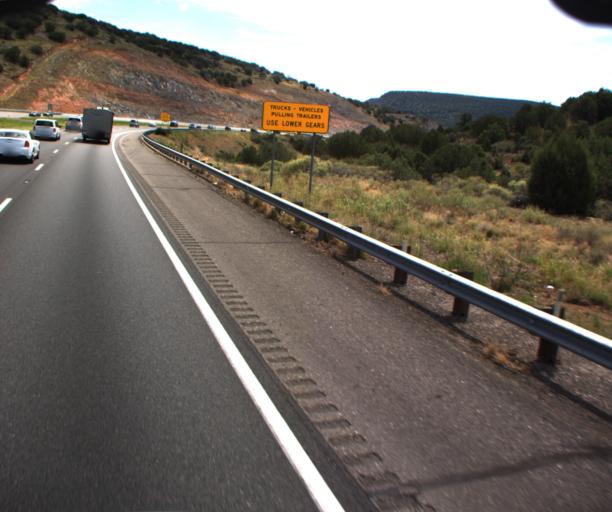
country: US
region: Arizona
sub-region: Yavapai County
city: Camp Verde
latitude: 34.5333
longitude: -111.9617
